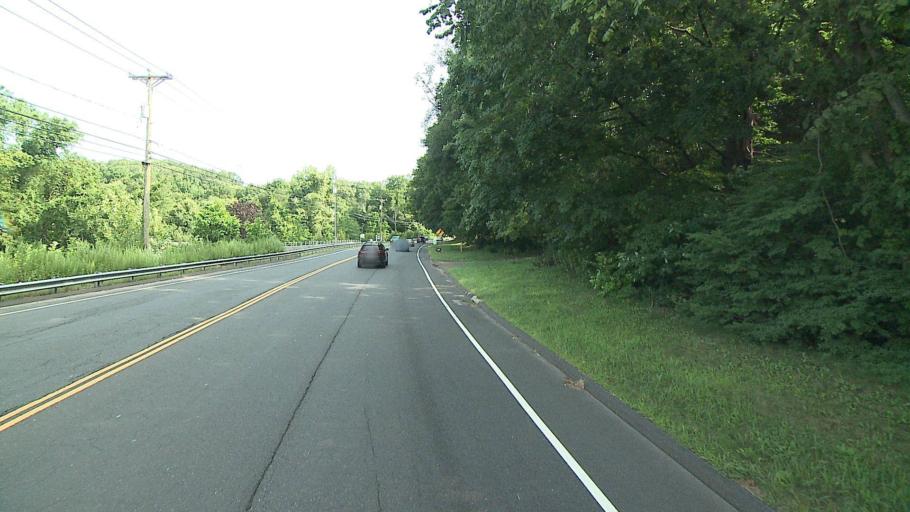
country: US
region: Connecticut
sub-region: Fairfield County
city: Wilton
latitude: 41.2191
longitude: -73.4282
